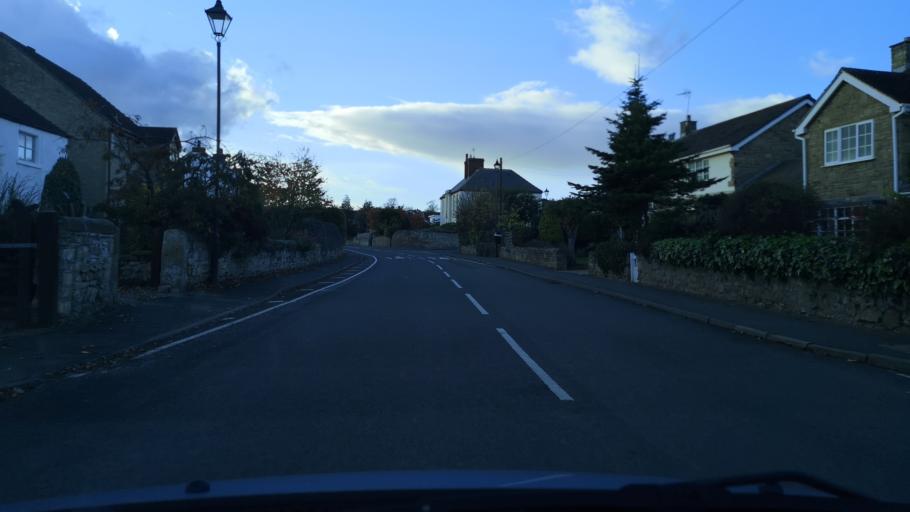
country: GB
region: England
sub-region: City and Borough of Wakefield
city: Darrington
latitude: 53.6745
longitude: -1.2662
